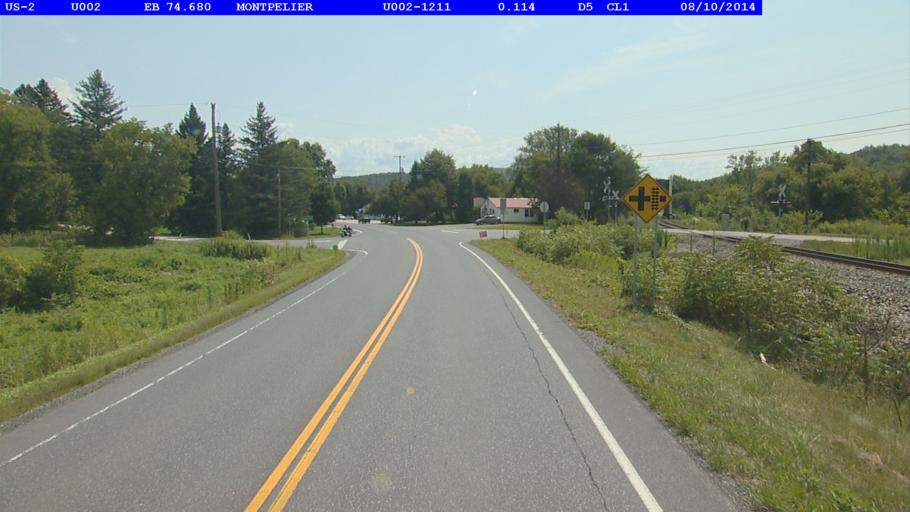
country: US
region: Vermont
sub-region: Washington County
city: Montpelier
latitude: 44.2595
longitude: -72.6095
